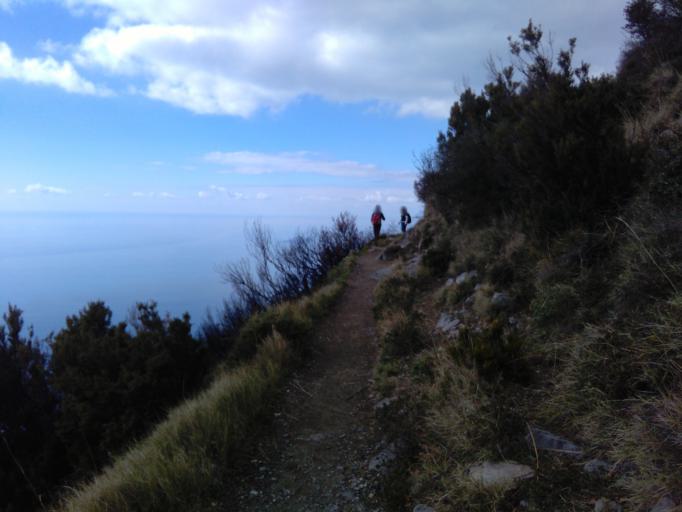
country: IT
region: Campania
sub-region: Provincia di Salerno
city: Praiano
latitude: 40.6221
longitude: 14.5187
